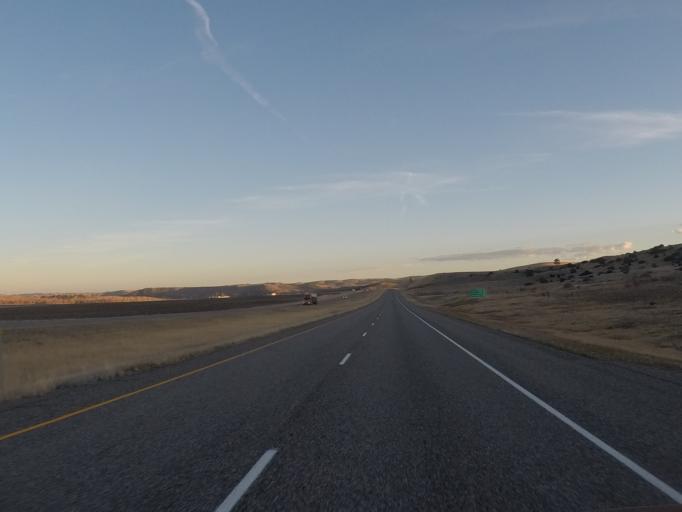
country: US
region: Montana
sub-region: Sweet Grass County
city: Big Timber
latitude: 45.7595
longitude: -109.7854
